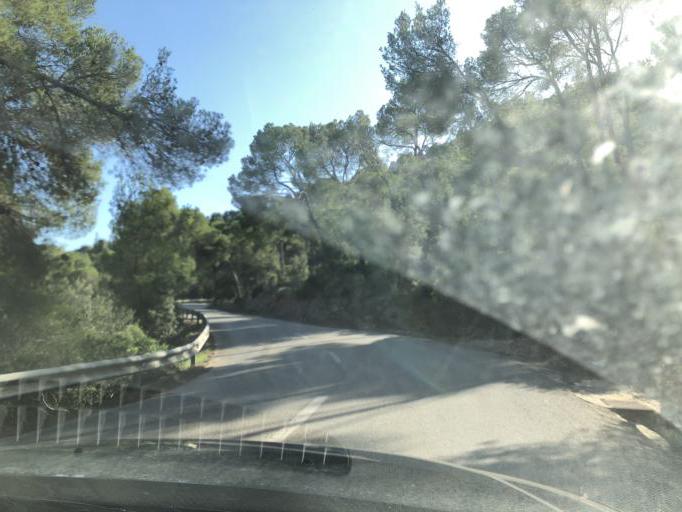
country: ES
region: Balearic Islands
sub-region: Illes Balears
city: Camp de Mar
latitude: 39.5422
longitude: 2.4017
